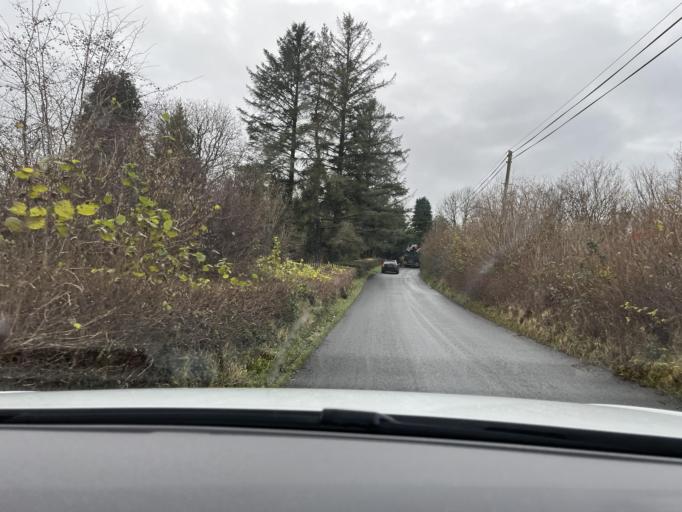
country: IE
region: Connaught
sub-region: County Leitrim
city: Manorhamilton
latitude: 54.2377
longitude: -8.2745
